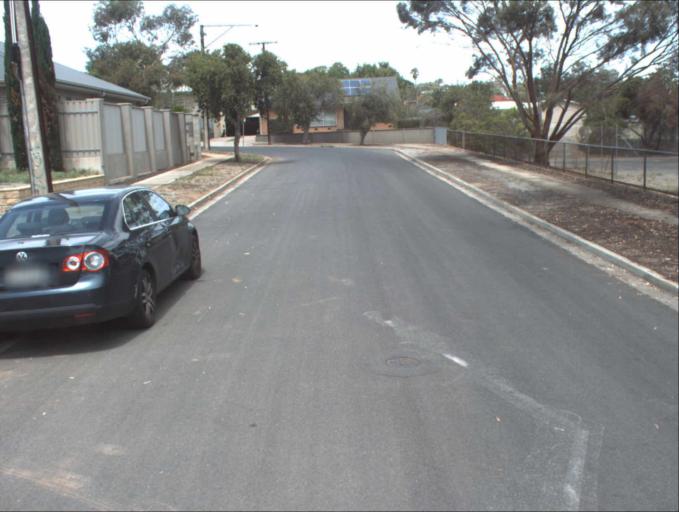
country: AU
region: South Australia
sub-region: Port Adelaide Enfield
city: Enfield
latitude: -34.8495
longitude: 138.6062
